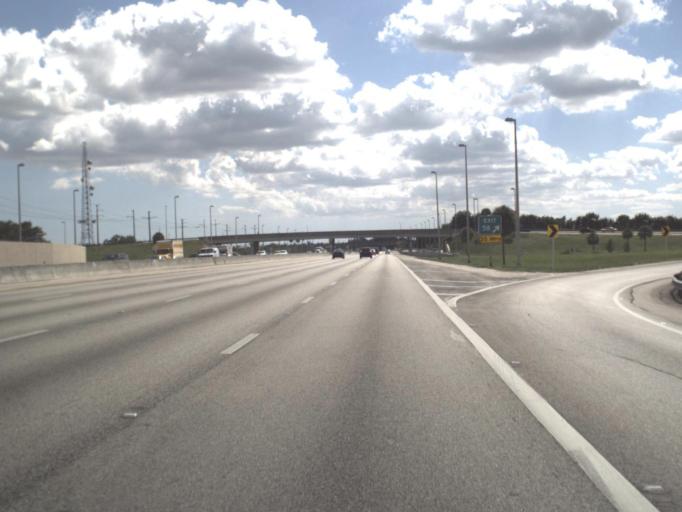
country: US
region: Florida
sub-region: Broward County
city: Lauderhill
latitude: 26.1425
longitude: -80.2195
